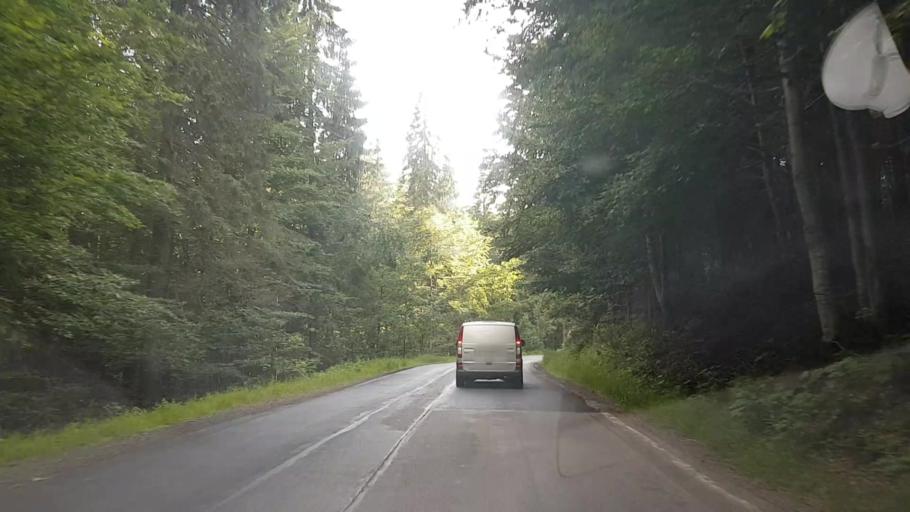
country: RO
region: Harghita
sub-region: Comuna Varsag
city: Varsag
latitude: 46.6656
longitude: 25.3087
